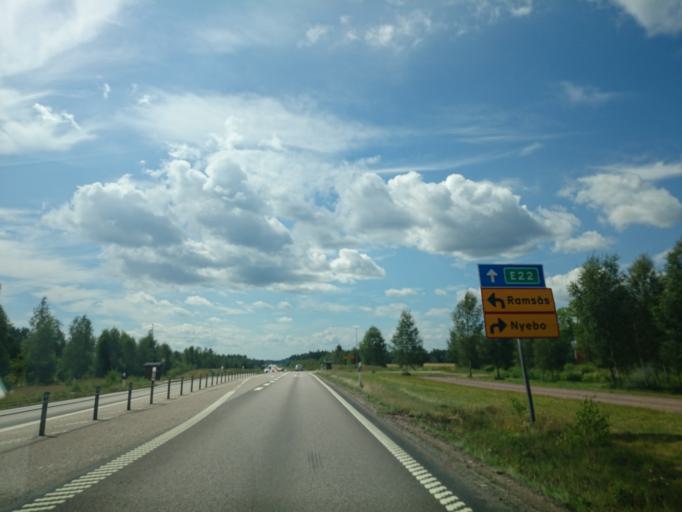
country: SE
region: Kalmar
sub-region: Monsteras Kommun
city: Timmernabben
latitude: 56.9865
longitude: 16.4071
